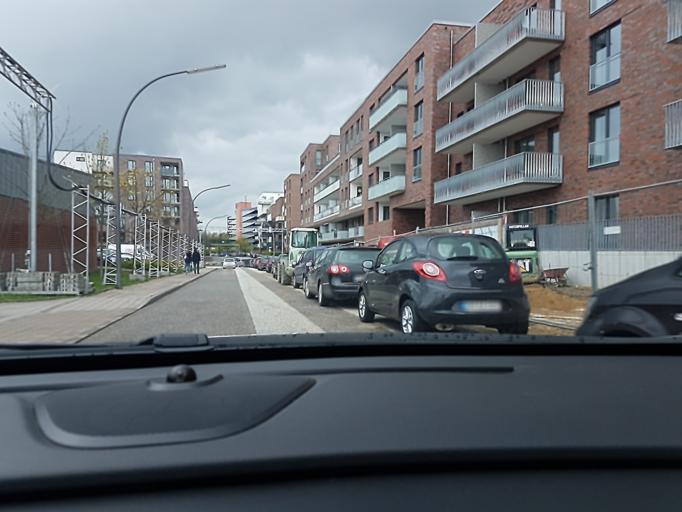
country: DE
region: Hamburg
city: Altona
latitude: 53.5571
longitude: 9.9044
